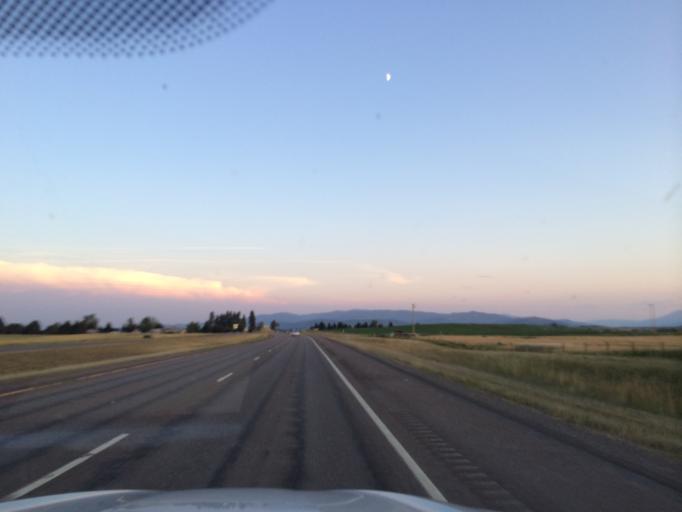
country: US
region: Montana
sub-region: Flathead County
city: Evergreen
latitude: 48.2712
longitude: -114.3307
